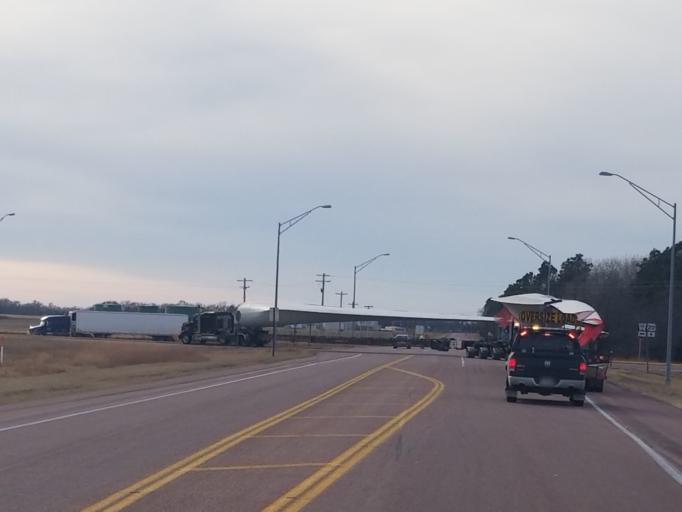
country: US
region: Nebraska
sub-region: Knox County
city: Creighton
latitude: 42.3478
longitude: -98.0269
